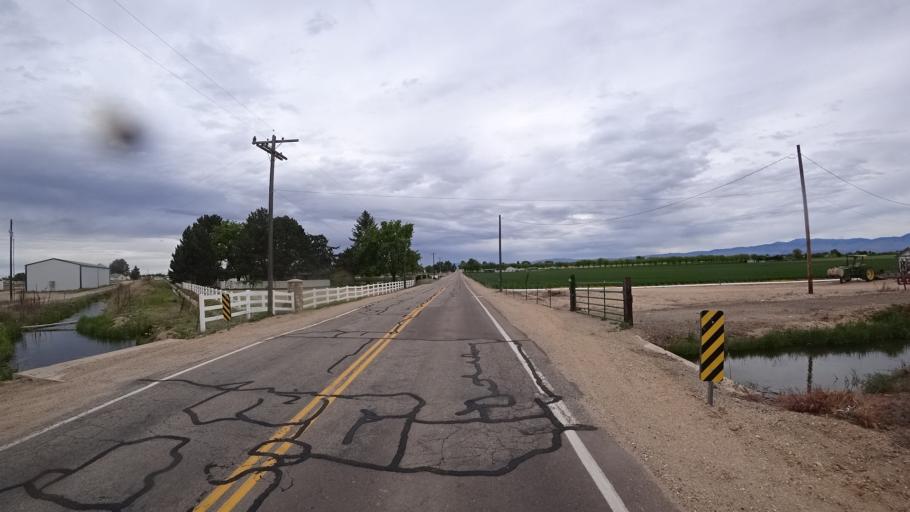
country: US
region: Idaho
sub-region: Ada County
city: Meridian
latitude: 43.5666
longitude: -116.4137
